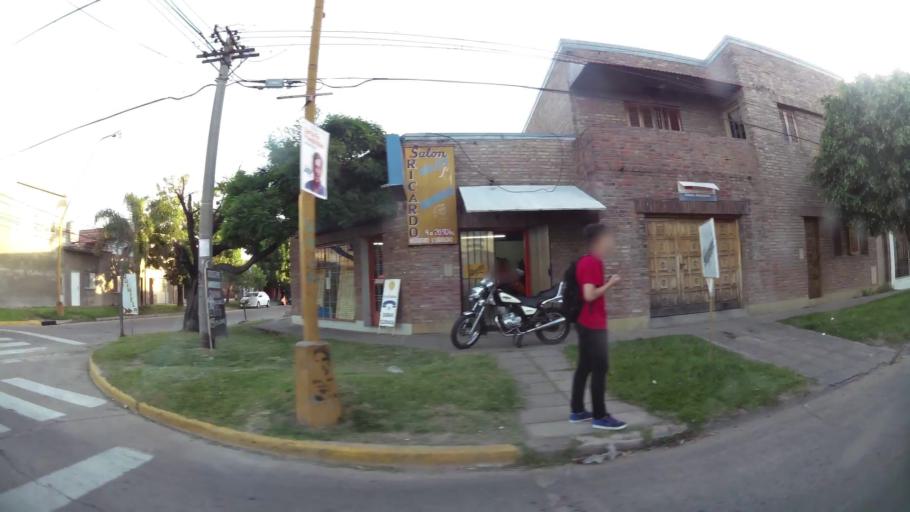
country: AR
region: Santa Fe
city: Santa Fe de la Vera Cruz
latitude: -31.6004
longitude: -60.6857
